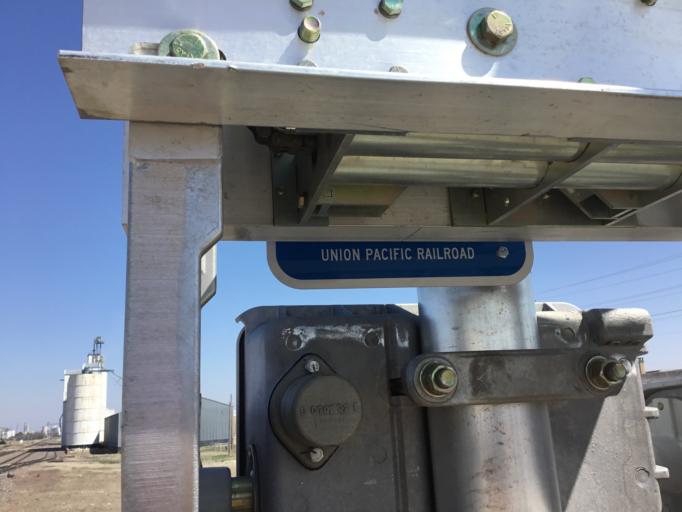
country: US
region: Kansas
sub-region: Russell County
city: Russell
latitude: 38.8941
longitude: -98.8623
